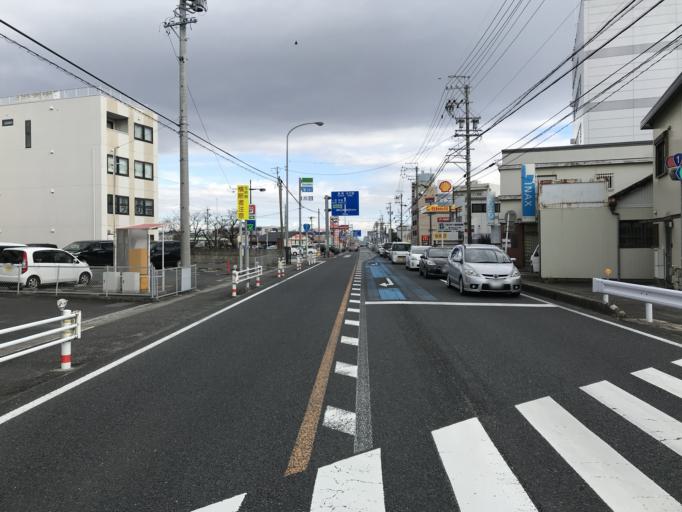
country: JP
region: Aichi
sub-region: Aisai-shi
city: Aisai
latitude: 35.1123
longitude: 136.7283
